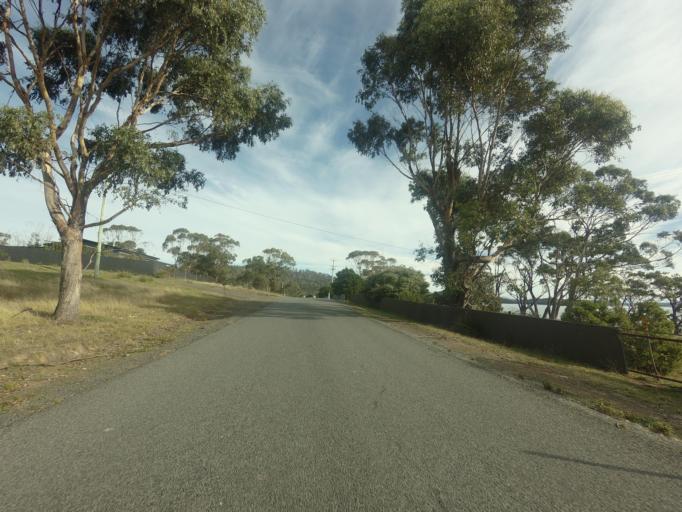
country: AU
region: Tasmania
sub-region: Sorell
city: Sorell
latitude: -42.9520
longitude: 147.8511
